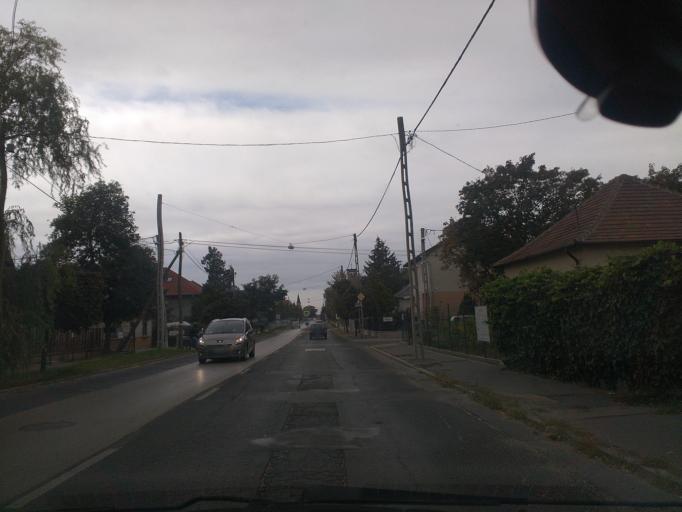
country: HU
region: Pest
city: Gyal
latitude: 47.4105
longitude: 19.1963
